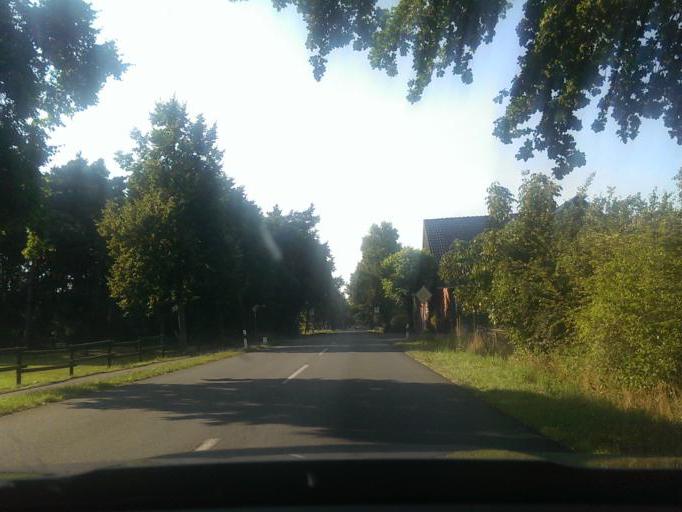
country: DE
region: North Rhine-Westphalia
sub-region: Regierungsbezirk Detmold
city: Delbruck
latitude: 51.7491
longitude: 8.5812
